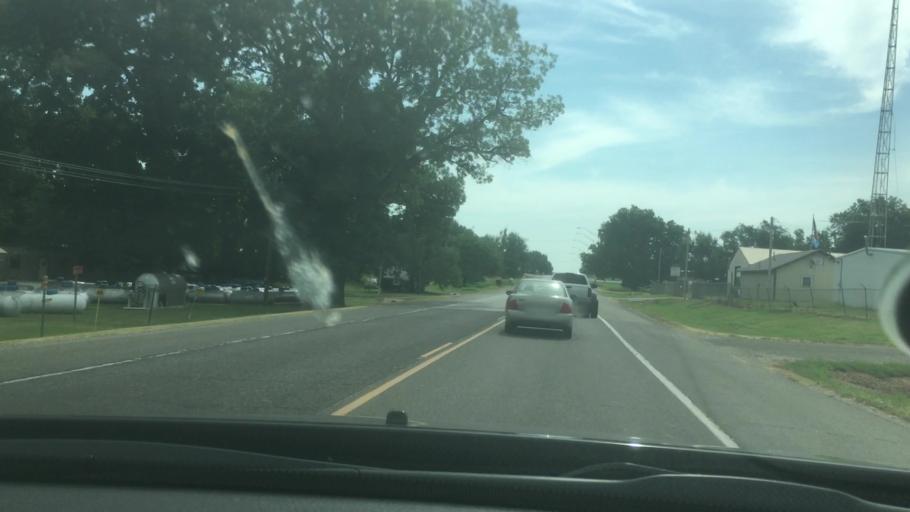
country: US
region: Oklahoma
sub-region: Garvin County
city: Maysville
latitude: 34.8173
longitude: -97.4230
